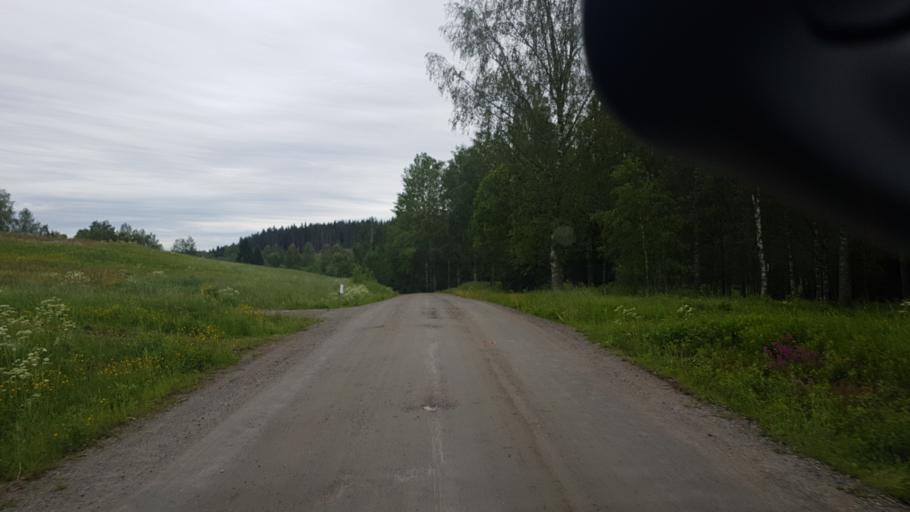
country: NO
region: Ostfold
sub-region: Romskog
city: Romskog
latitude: 59.6852
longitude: 11.9327
